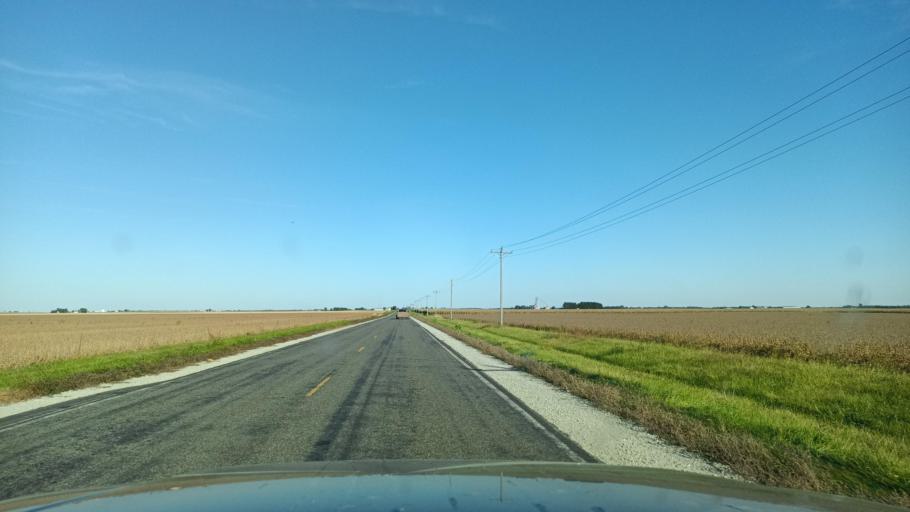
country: US
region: Illinois
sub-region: McLean County
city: Le Roy
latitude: 40.2242
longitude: -88.7801
